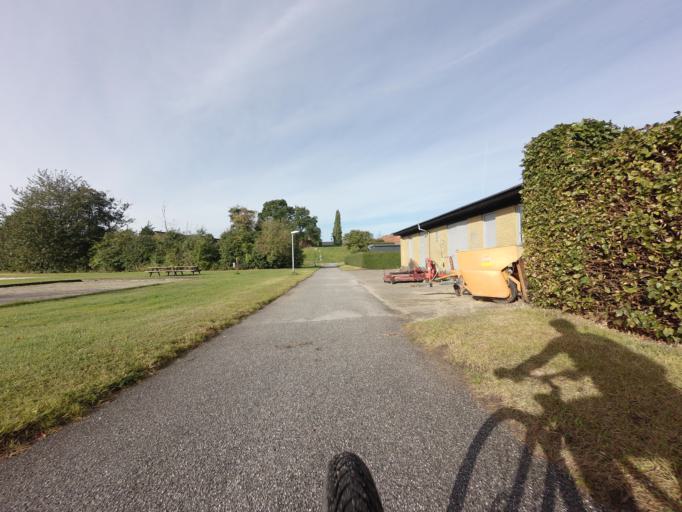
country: DK
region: Central Jutland
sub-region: Viborg Kommune
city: Viborg
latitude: 56.4277
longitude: 9.3969
